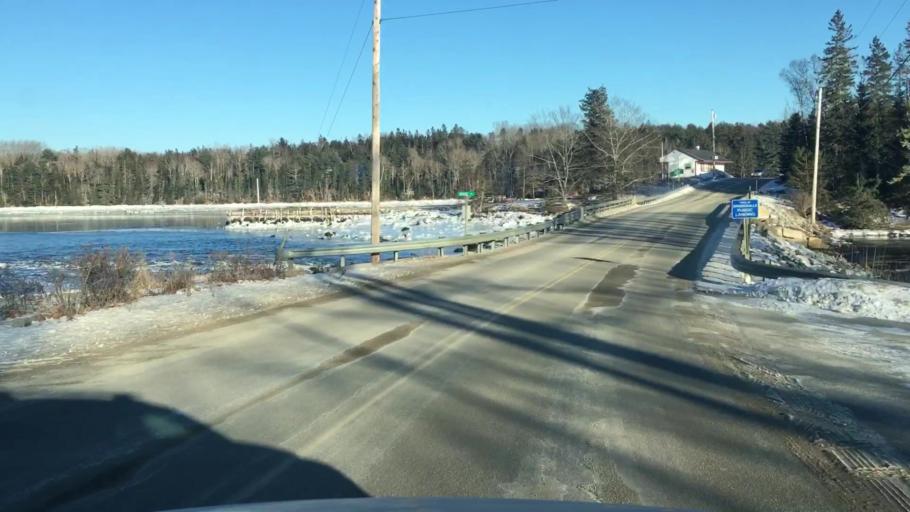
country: US
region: Maine
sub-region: Hancock County
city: Penobscot
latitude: 44.3980
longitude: -68.7056
